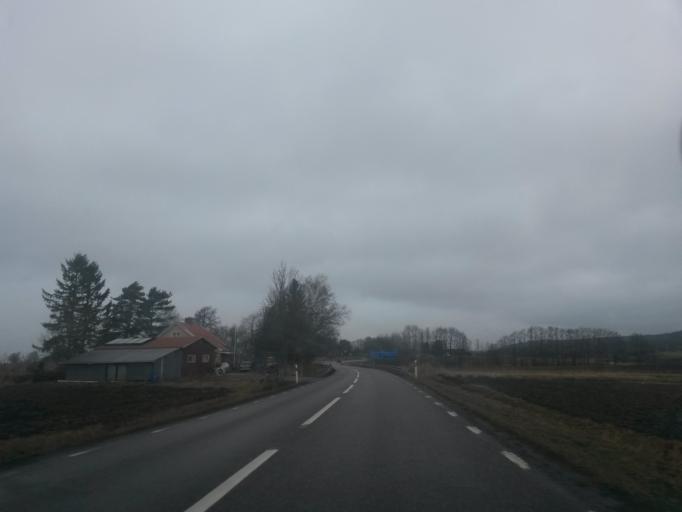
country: SE
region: Vaestra Goetaland
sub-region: Vanersborgs Kommun
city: Vargon
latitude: 58.2863
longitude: 12.3951
